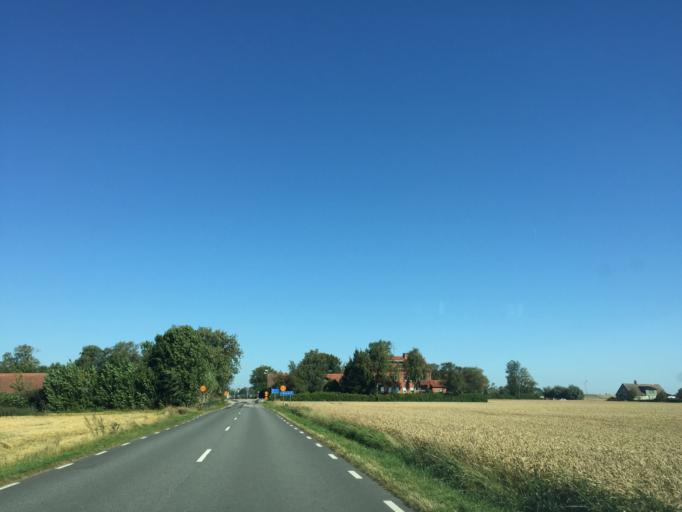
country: SE
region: Skane
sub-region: Ystads Kommun
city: Kopingebro
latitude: 55.4269
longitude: 14.1138
